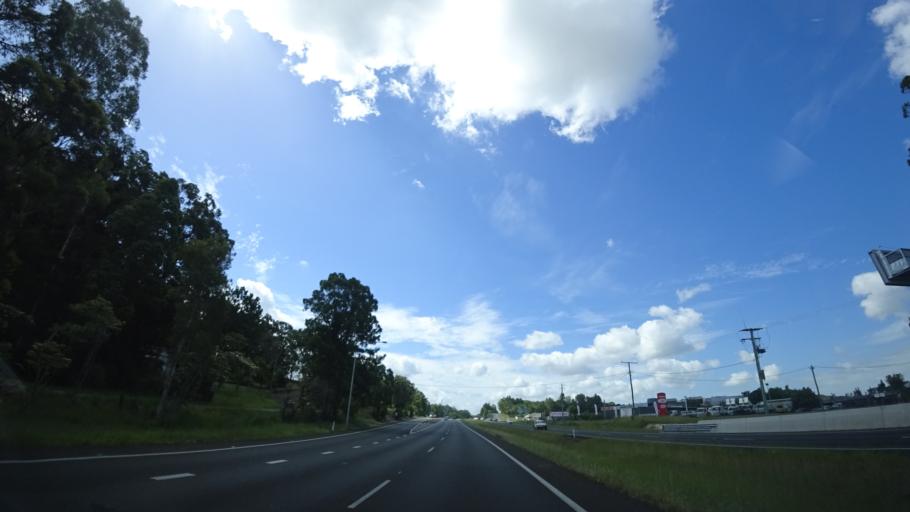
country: AU
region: Queensland
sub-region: Sunshine Coast
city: Woombye
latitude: -26.6798
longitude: 153.0021
